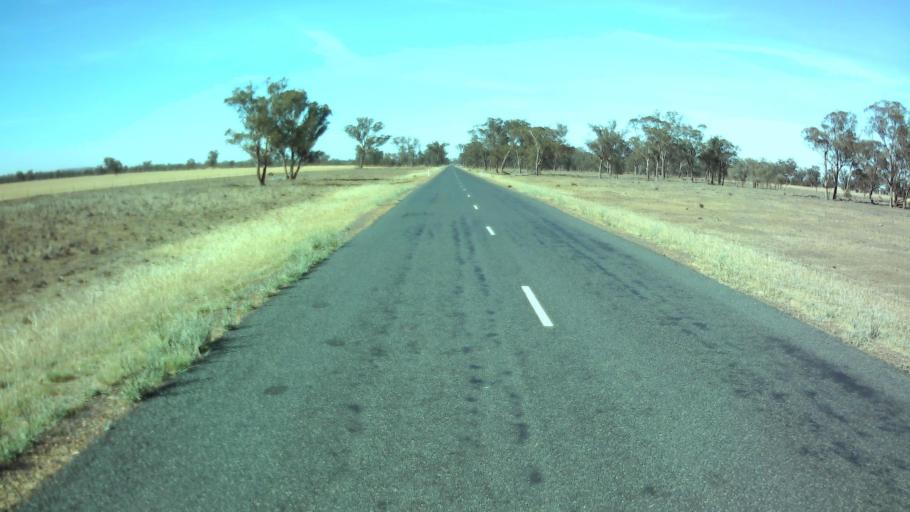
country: AU
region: New South Wales
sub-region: Weddin
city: Grenfell
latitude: -34.0861
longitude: 147.8924
